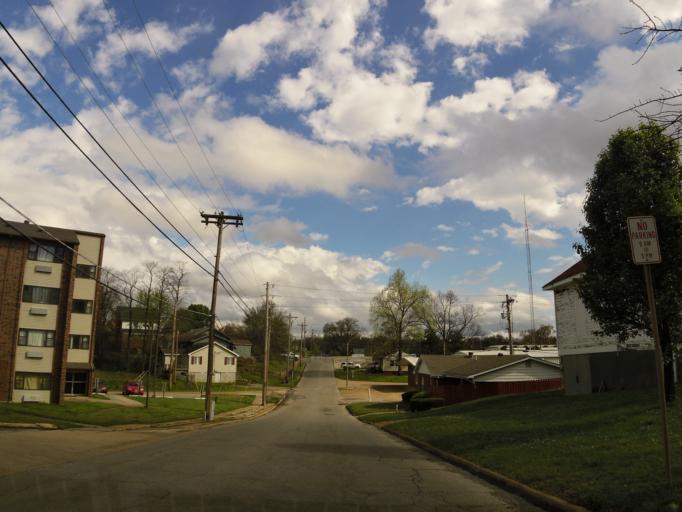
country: US
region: Missouri
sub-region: Butler County
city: Poplar Bluff
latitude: 36.7588
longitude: -90.3914
